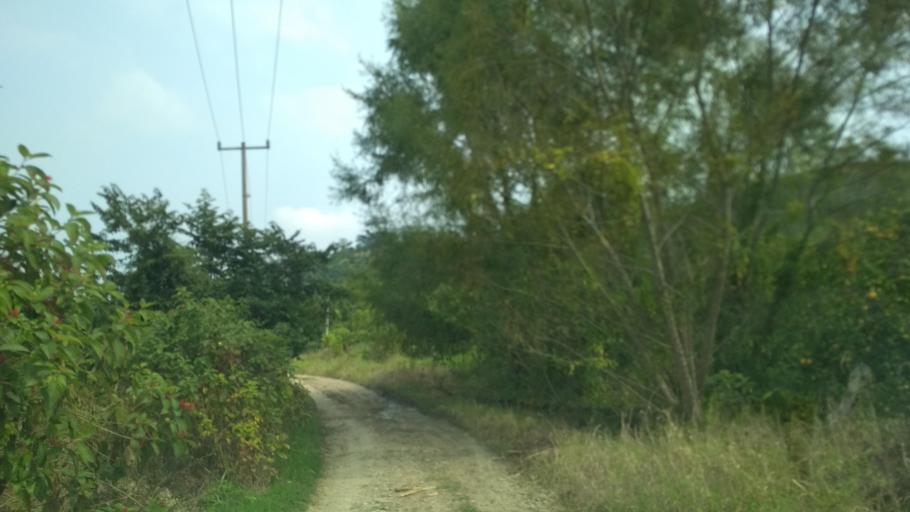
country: MM
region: Kayah
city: Loikaw
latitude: 20.2078
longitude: 97.3162
